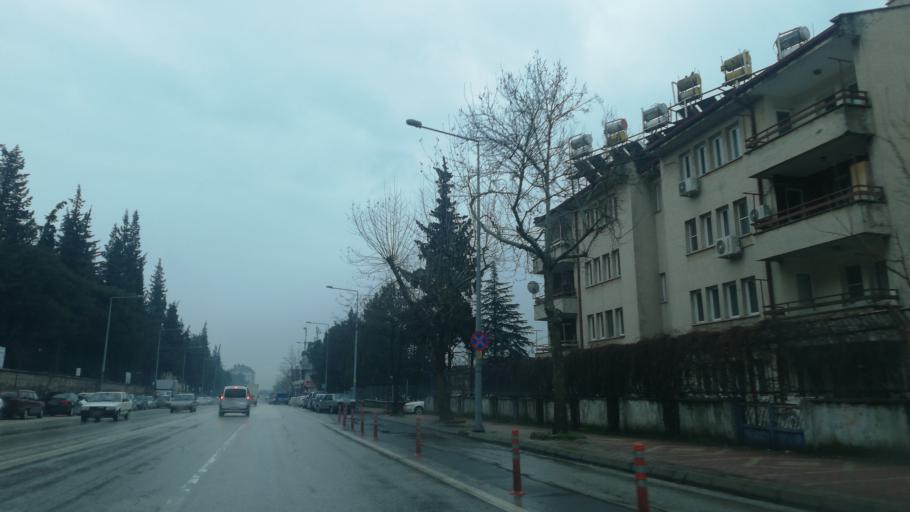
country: TR
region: Kahramanmaras
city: Kahramanmaras
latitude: 37.5761
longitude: 36.9351
